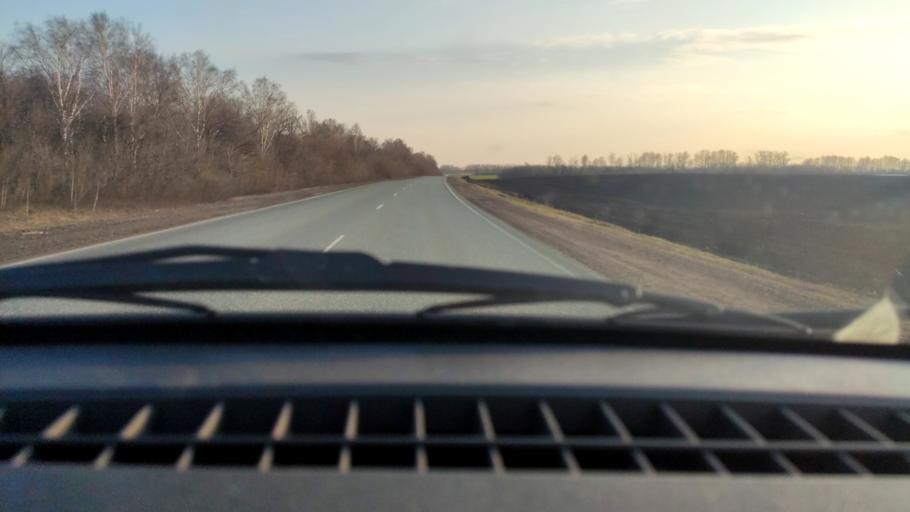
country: RU
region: Bashkortostan
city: Chishmy
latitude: 54.5031
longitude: 55.2869
